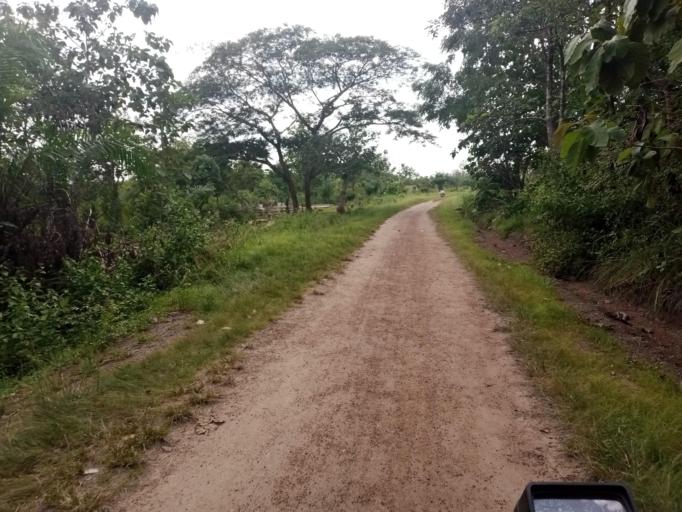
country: TG
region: Maritime
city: Tsevie
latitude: 6.5232
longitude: 1.0565
